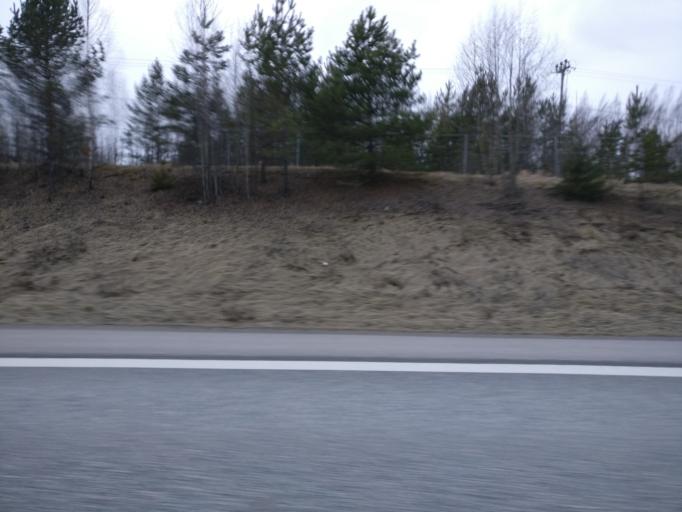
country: FI
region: Uusimaa
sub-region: Helsinki
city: Nurmijaervi
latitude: 60.3612
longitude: 24.8082
